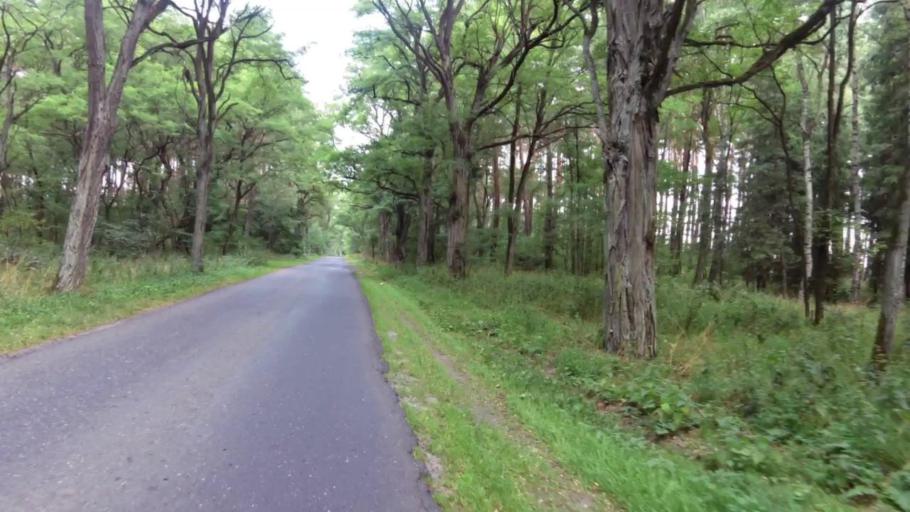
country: PL
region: West Pomeranian Voivodeship
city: Trzcinsko Zdroj
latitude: 52.8579
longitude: 14.6439
